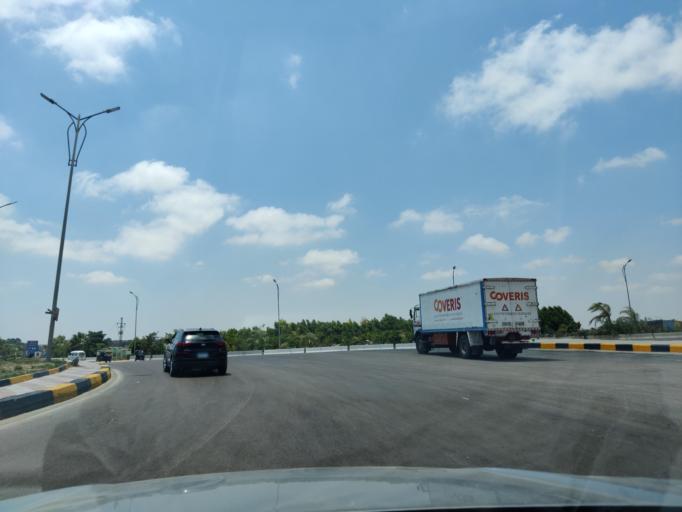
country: EG
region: Alexandria
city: Alexandria
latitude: 30.9757
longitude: 29.6610
